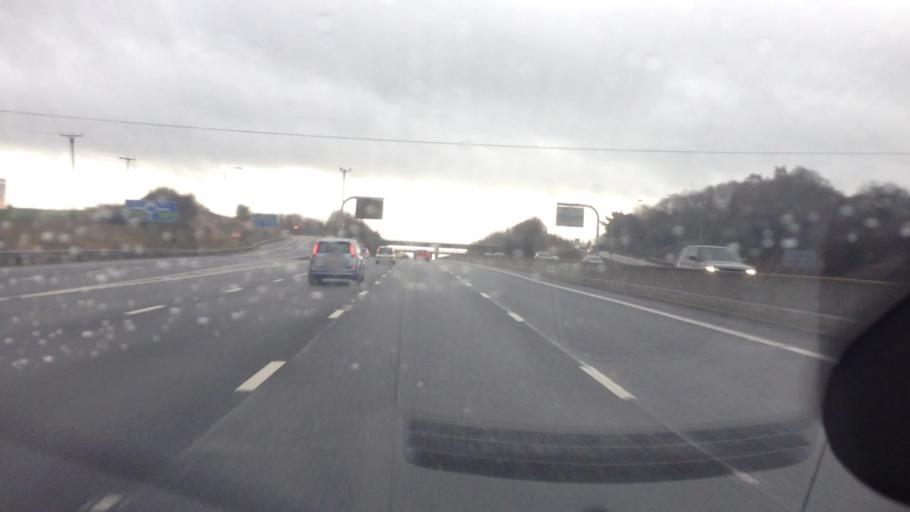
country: GB
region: England
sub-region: City and Borough of Wakefield
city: Ossett
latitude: 53.6873
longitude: -1.5559
